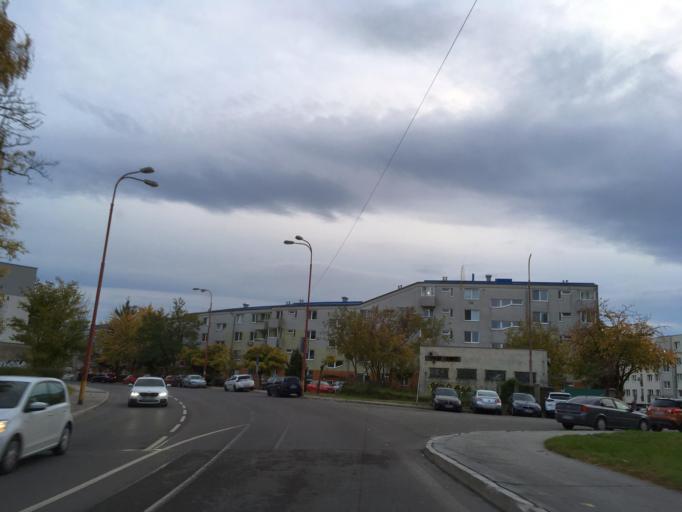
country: SK
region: Bratislavsky
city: Dunajska Luzna
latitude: 48.1405
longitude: 17.1966
